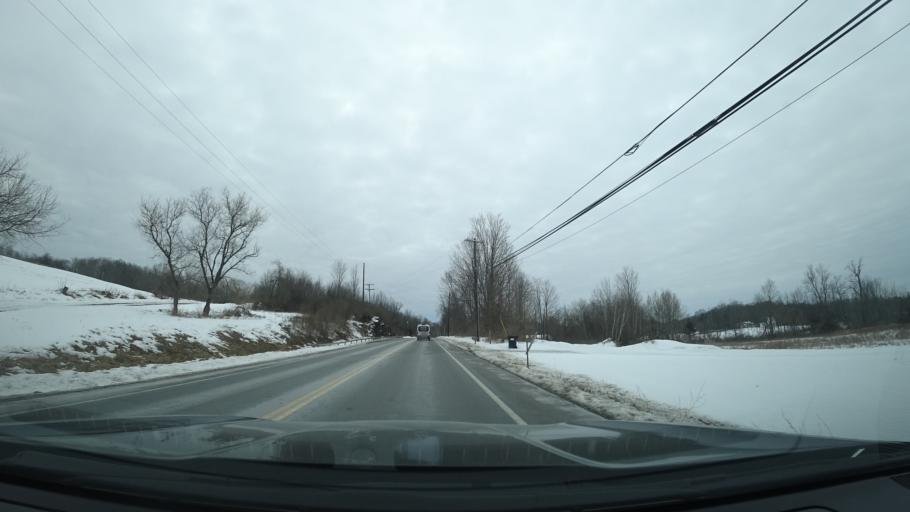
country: US
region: New York
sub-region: Washington County
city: Fort Edward
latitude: 43.2209
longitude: -73.4889
